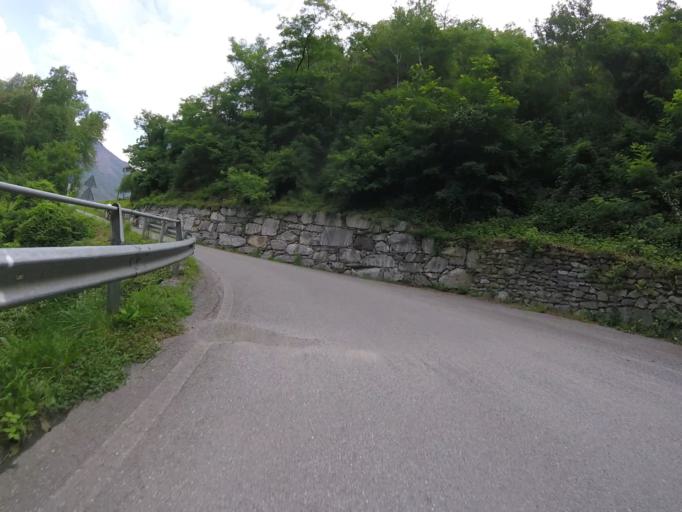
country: IT
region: Lombardy
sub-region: Provincia di Sondrio
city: Mazzo di Valtellina
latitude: 46.2537
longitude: 10.2625
